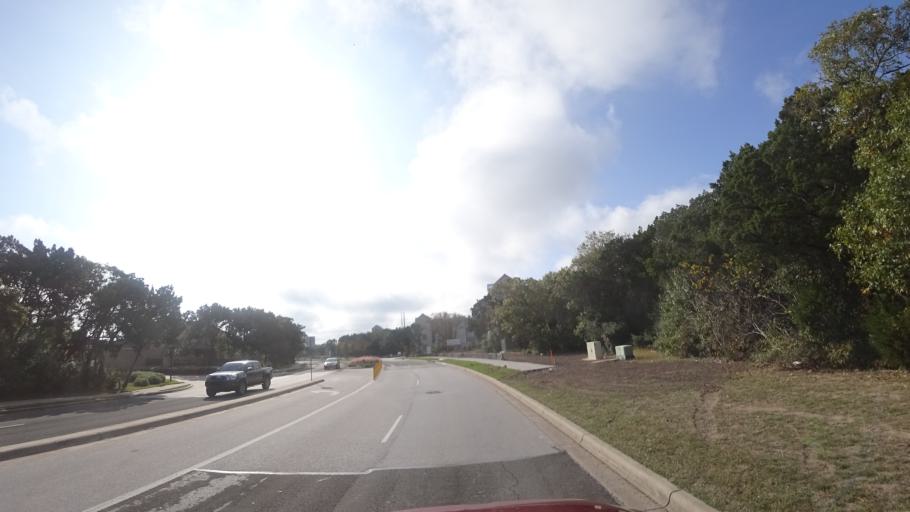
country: US
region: Texas
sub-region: Williamson County
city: Anderson Mill
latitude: 30.4008
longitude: -97.8466
